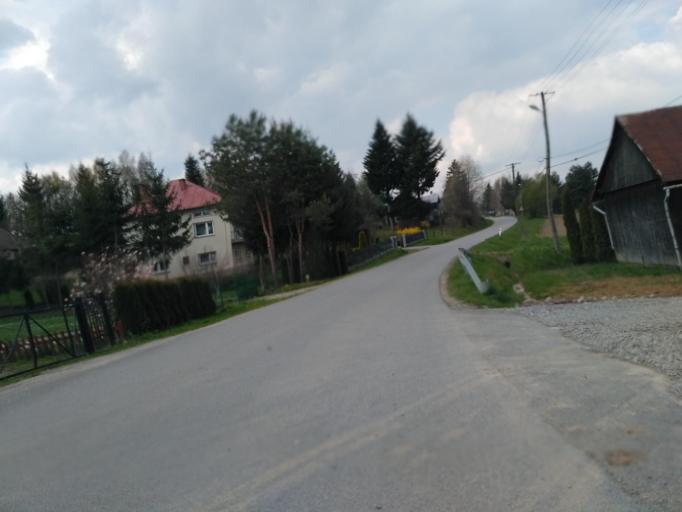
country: PL
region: Subcarpathian Voivodeship
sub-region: Powiat sanocki
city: Strachocina
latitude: 49.6049
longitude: 22.0906
